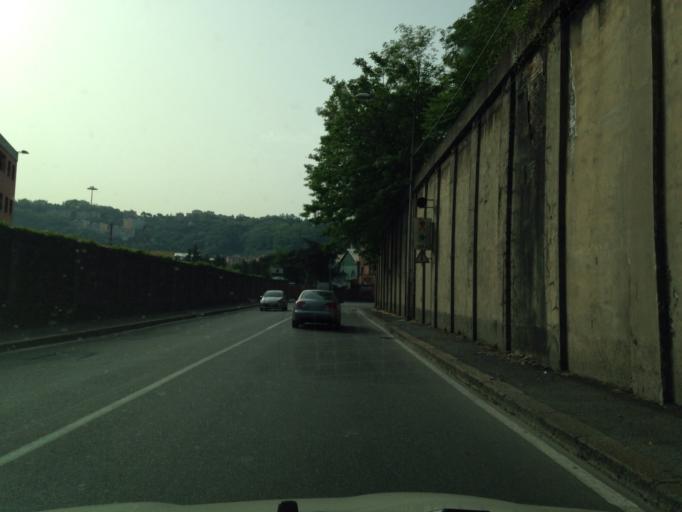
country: IT
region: Liguria
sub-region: Provincia di Genova
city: San Teodoro
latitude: 44.4261
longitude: 8.8819
